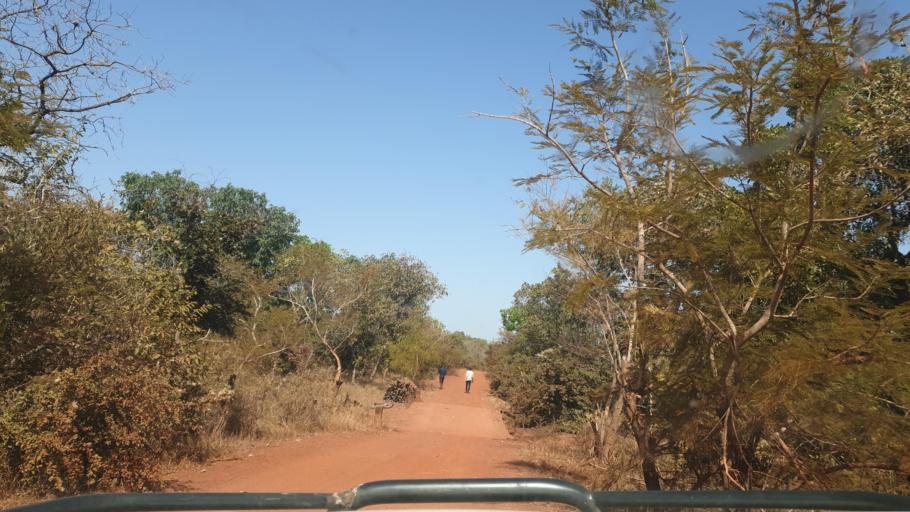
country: ML
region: Koulikoro
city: Dioila
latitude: 11.9234
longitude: -6.9842
